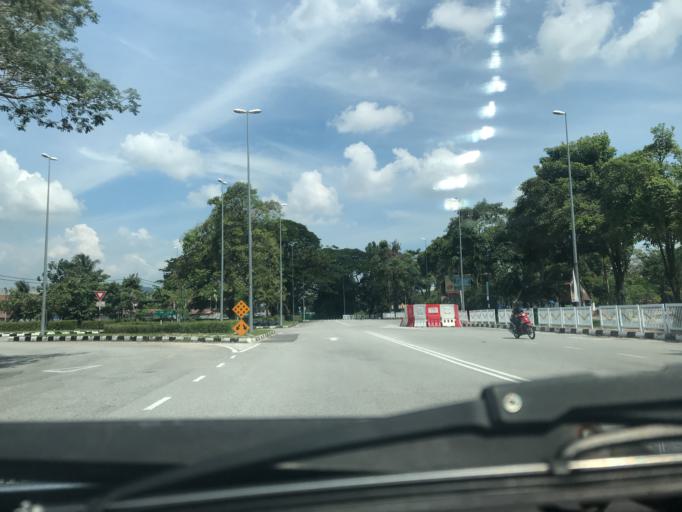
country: MY
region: Perak
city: Ipoh
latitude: 4.6063
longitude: 101.0991
